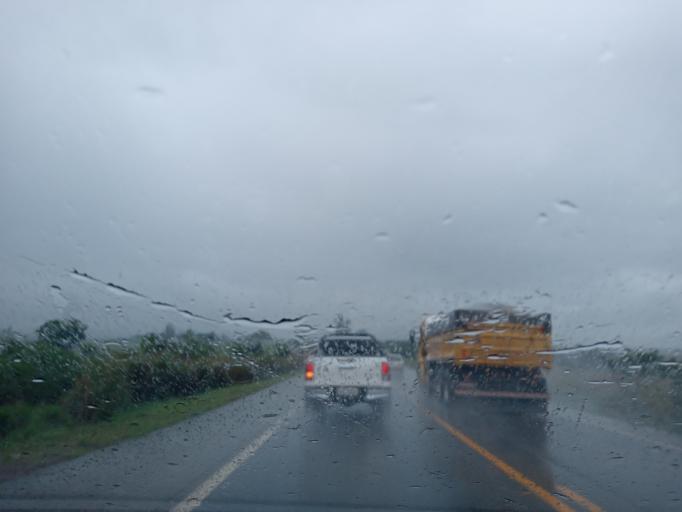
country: BR
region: Minas Gerais
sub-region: Luz
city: Luz
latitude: -19.7756
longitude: -45.7534
